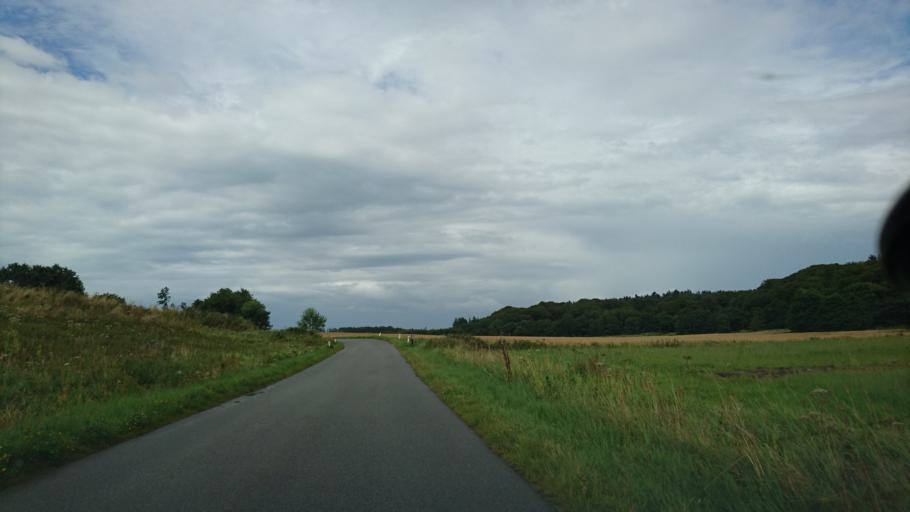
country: DK
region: North Denmark
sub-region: Frederikshavn Kommune
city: Frederikshavn
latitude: 57.4118
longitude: 10.4898
